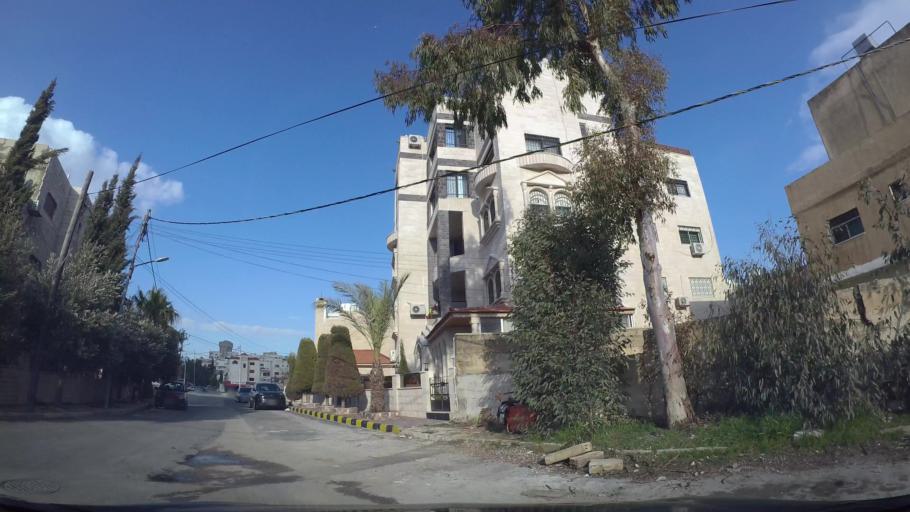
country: JO
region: Amman
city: Al Bunayyat ash Shamaliyah
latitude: 31.9080
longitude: 35.8810
